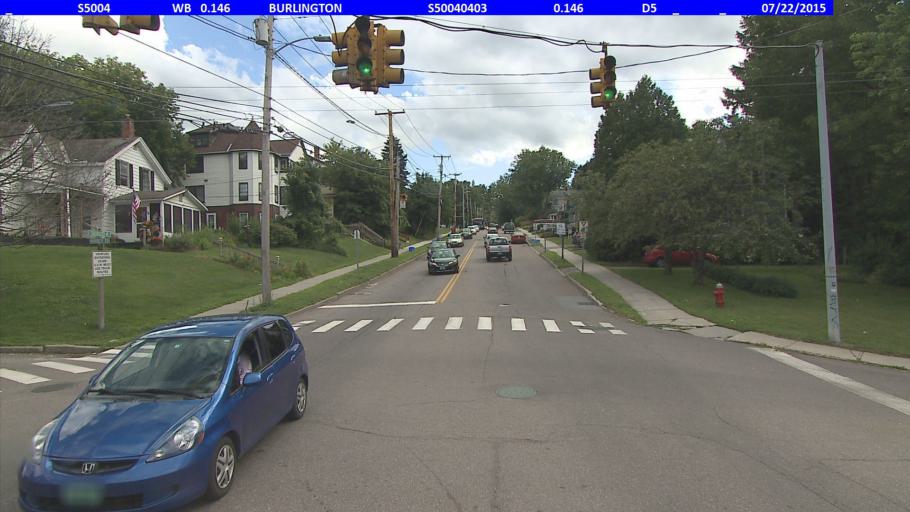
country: US
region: Vermont
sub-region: Chittenden County
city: Winooski
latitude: 44.4880
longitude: -73.1867
